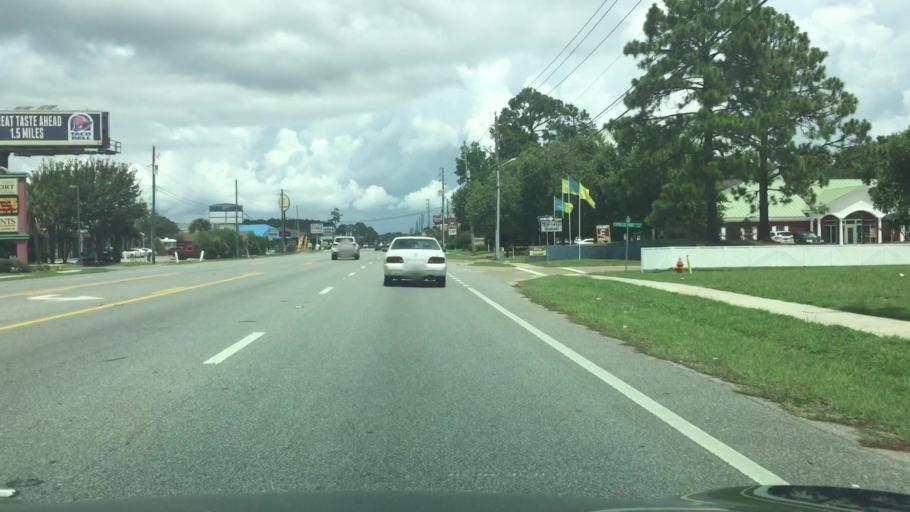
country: US
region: Florida
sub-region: Bay County
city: Upper Grand Lagoon
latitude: 30.1639
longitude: -85.7555
